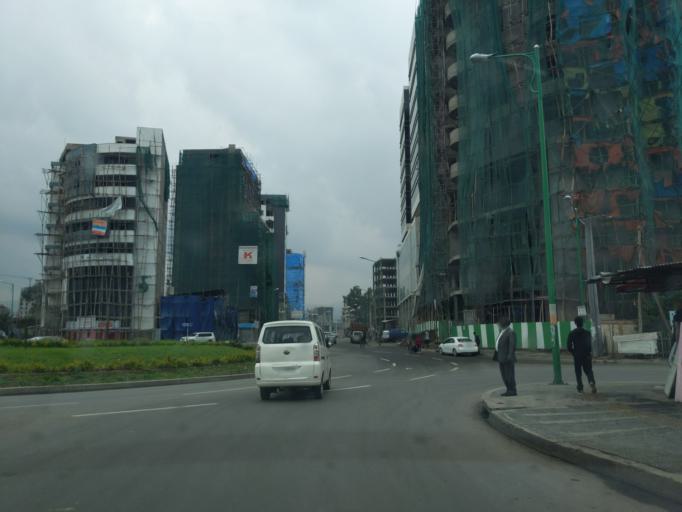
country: ET
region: Adis Abeba
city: Addis Ababa
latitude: 9.0000
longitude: 38.7670
